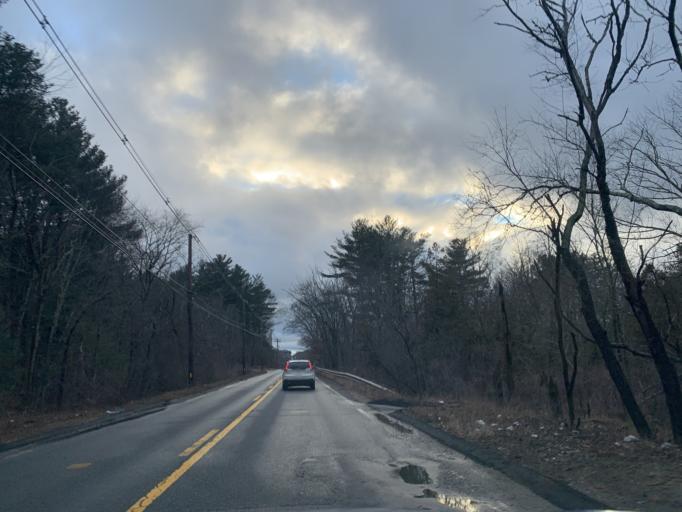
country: US
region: Massachusetts
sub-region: Norfolk County
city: Norfolk
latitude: 42.0955
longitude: -71.2936
